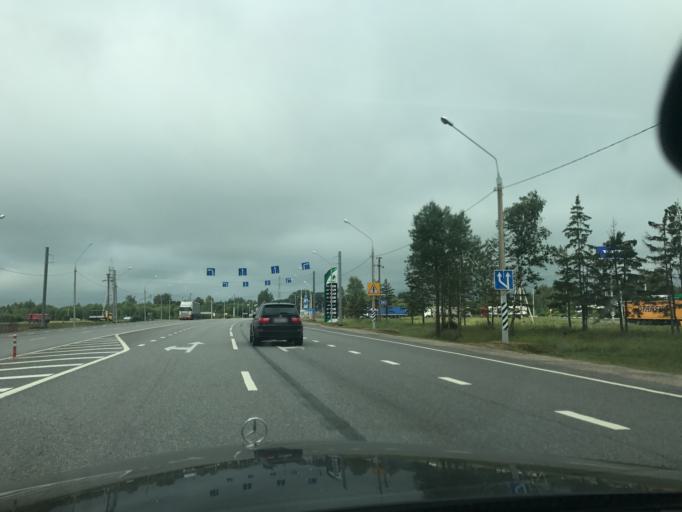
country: RU
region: Smolensk
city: Pechersk
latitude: 54.8520
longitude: 31.8622
